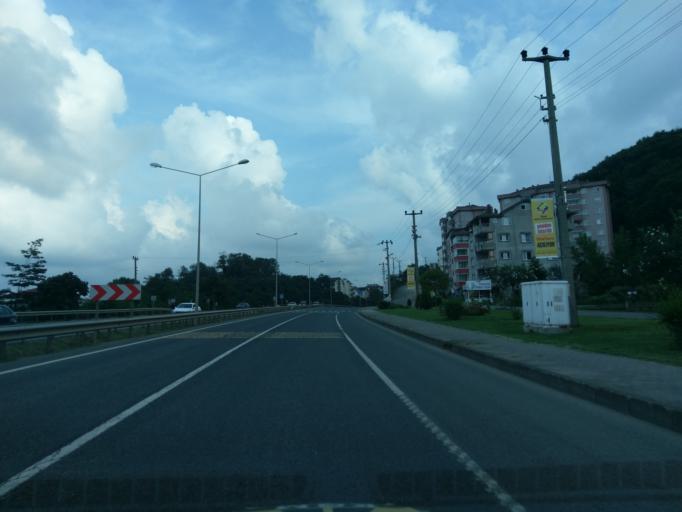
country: TR
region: Ordu
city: Fatsa
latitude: 41.0616
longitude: 37.4741
